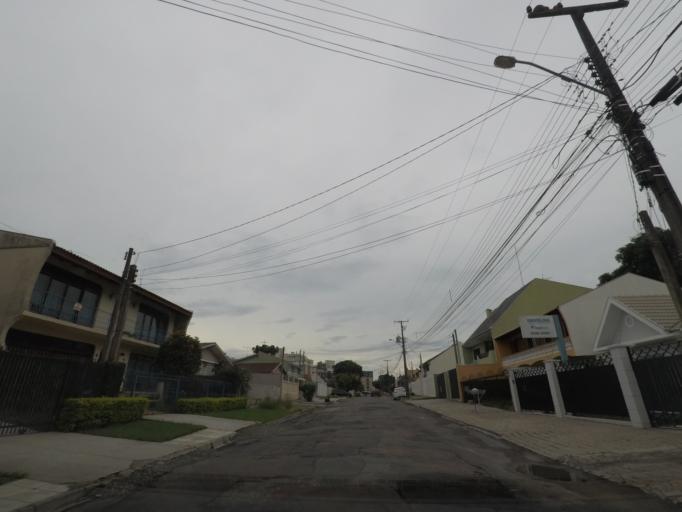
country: BR
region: Parana
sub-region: Curitiba
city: Curitiba
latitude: -25.4743
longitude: -49.2980
